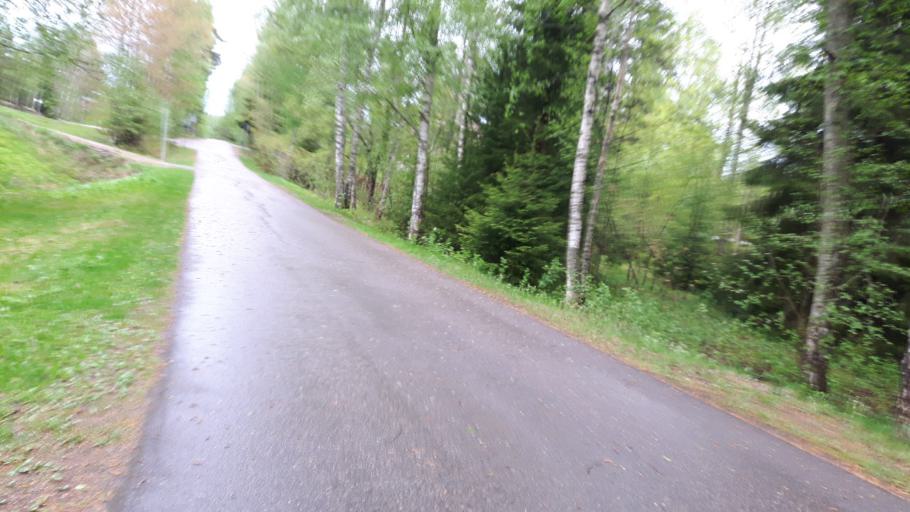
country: FI
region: Kymenlaakso
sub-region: Kotka-Hamina
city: Karhula
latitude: 60.5557
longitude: 26.9922
